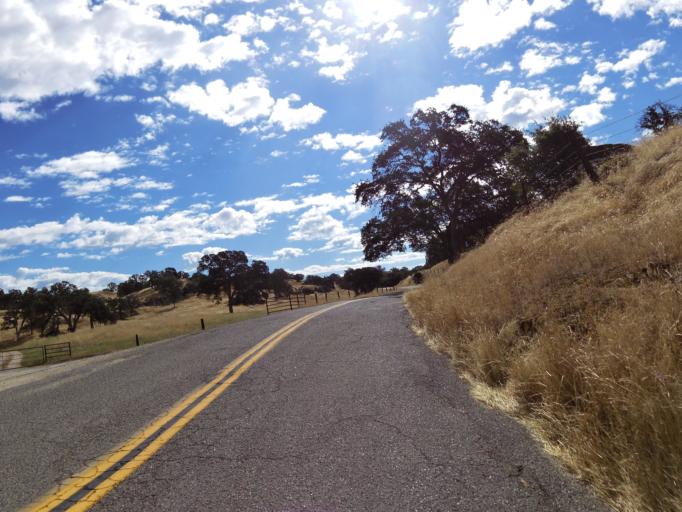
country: US
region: California
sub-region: Madera County
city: Yosemite Lakes
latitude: 37.0570
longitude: -119.7384
